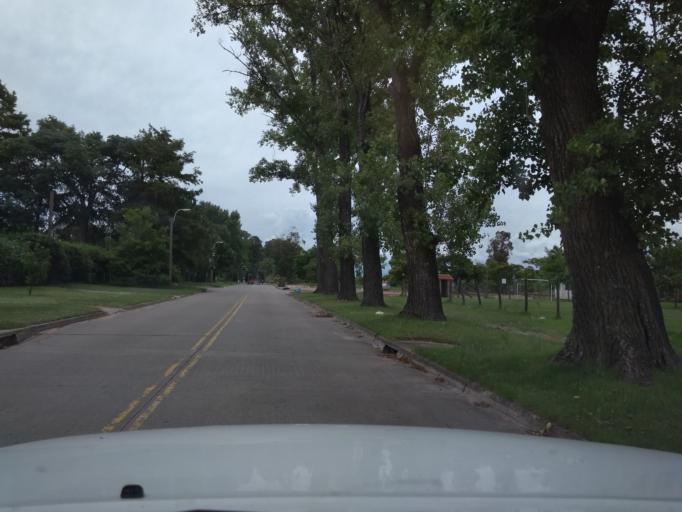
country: UY
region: Canelones
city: Paso de Carrasco
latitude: -34.8702
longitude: -56.0591
